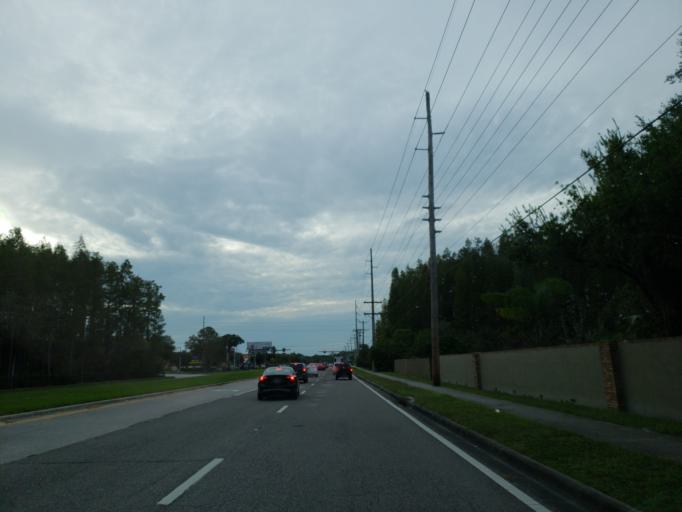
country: US
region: Florida
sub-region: Hillsborough County
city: Carrollwood Village
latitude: 28.0631
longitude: -82.5475
